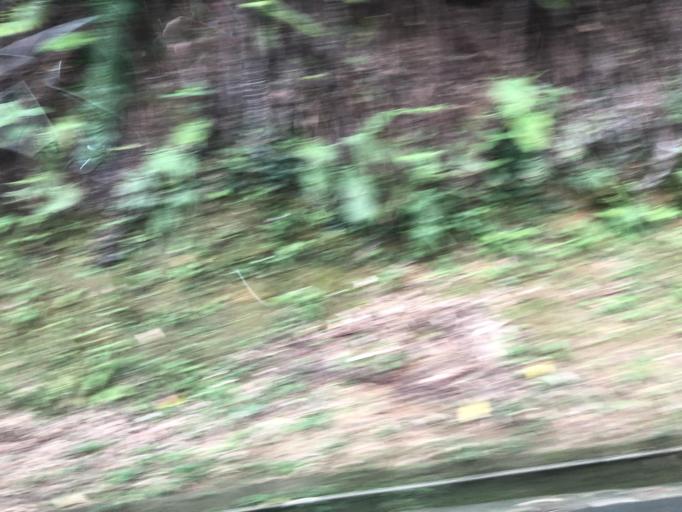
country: TW
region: Taiwan
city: Daxi
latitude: 24.9065
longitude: 121.3977
